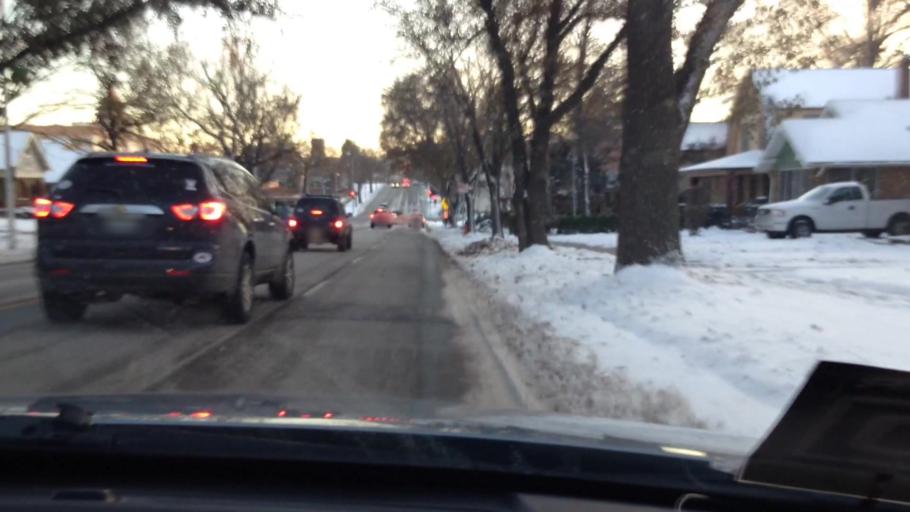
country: US
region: Kansas
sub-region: Johnson County
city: Mission Hills
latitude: 39.0150
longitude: -94.5768
